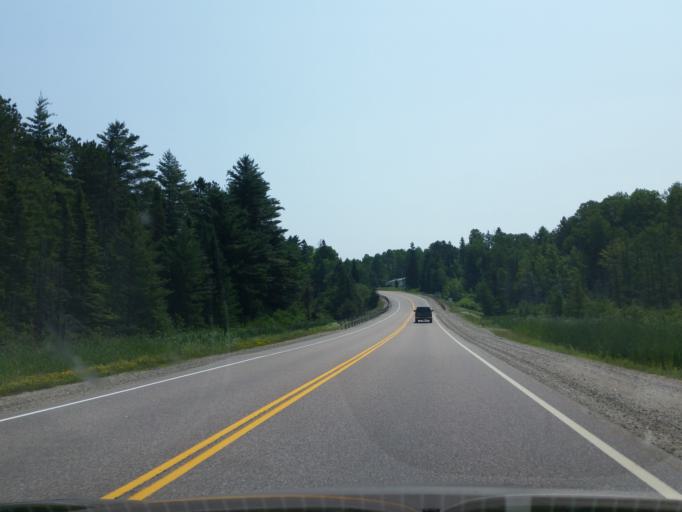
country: CA
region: Ontario
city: Deep River
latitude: 46.1726
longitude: -77.7073
